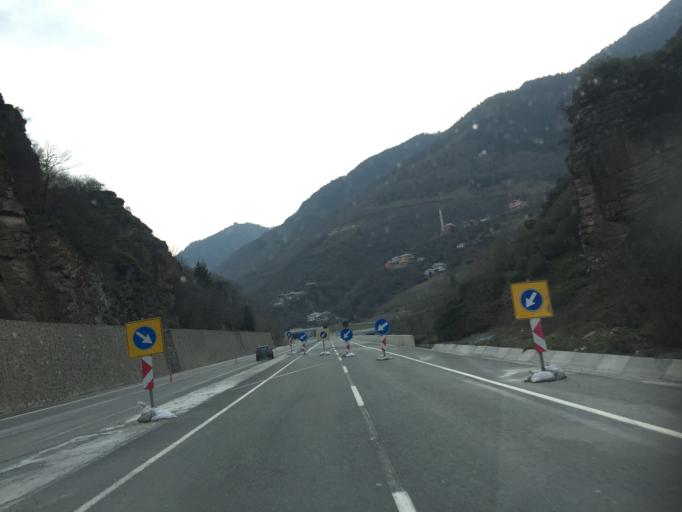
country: TR
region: Trabzon
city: Macka
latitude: 40.7827
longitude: 39.5732
